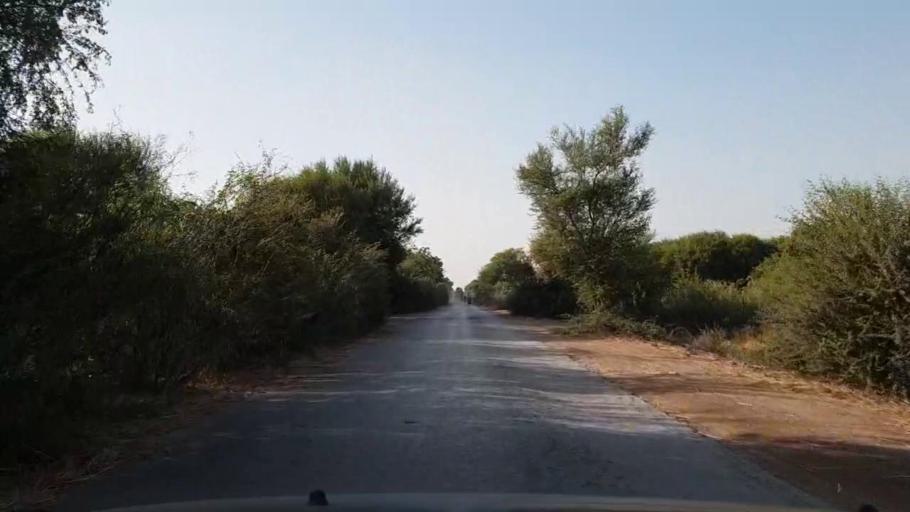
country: PK
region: Sindh
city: Tando Ghulam Ali
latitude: 25.1975
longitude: 68.7994
